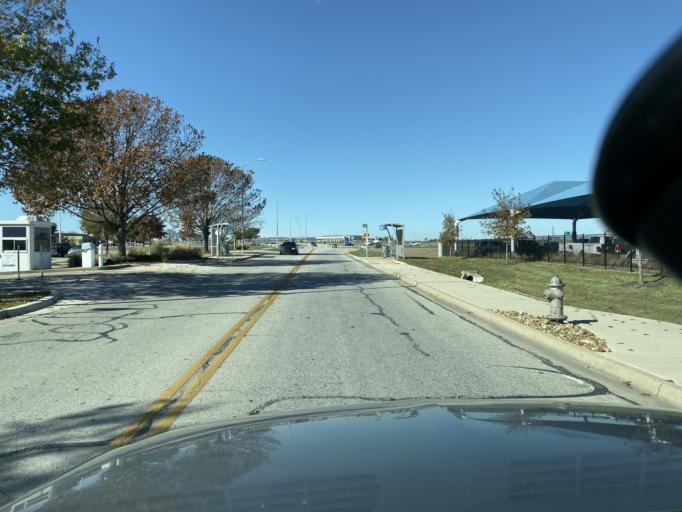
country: US
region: Texas
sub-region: Travis County
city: Hornsby Bend
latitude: 30.2123
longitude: -97.6635
